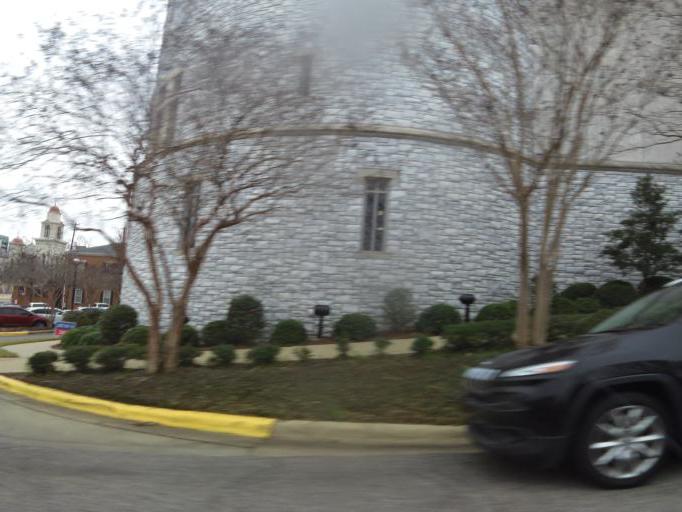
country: US
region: Alabama
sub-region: Montgomery County
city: Montgomery
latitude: 32.3745
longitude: -86.3072
